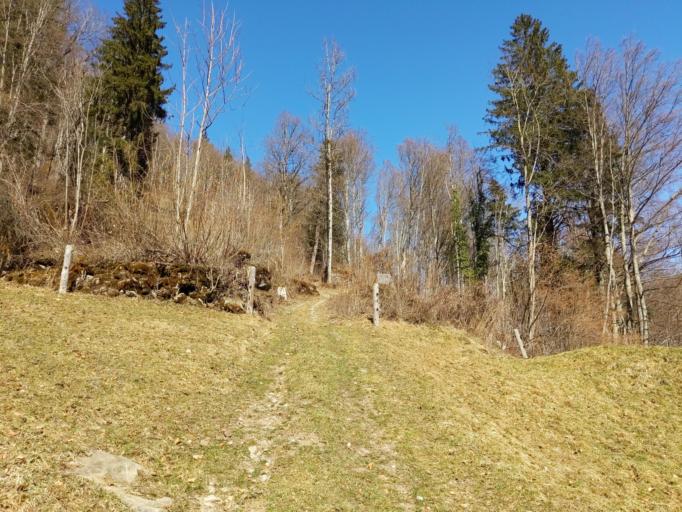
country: CH
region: Glarus
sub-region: Glarus
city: Luchsingen
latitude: 46.9457
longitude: 9.0168
